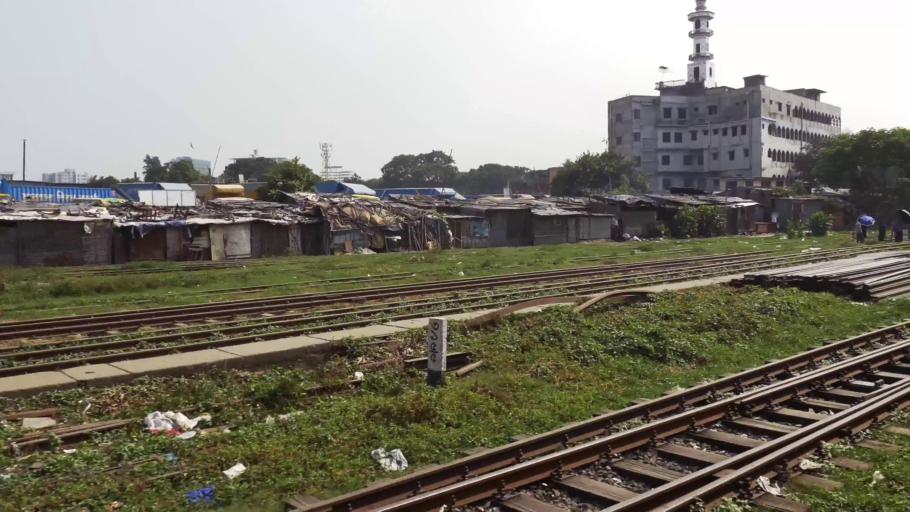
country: BD
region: Dhaka
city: Paltan
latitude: 23.7681
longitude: 90.3959
